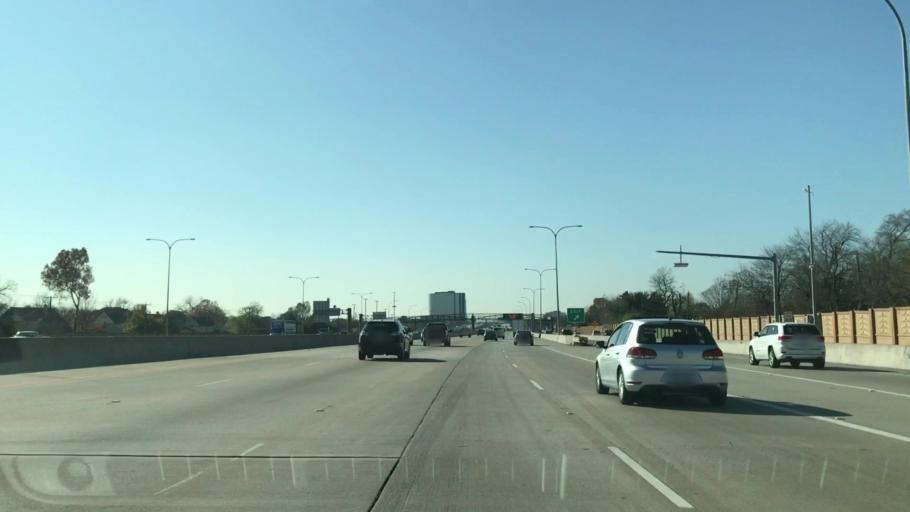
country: US
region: Texas
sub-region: Dallas County
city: Farmers Branch
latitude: 32.9167
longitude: -96.8598
